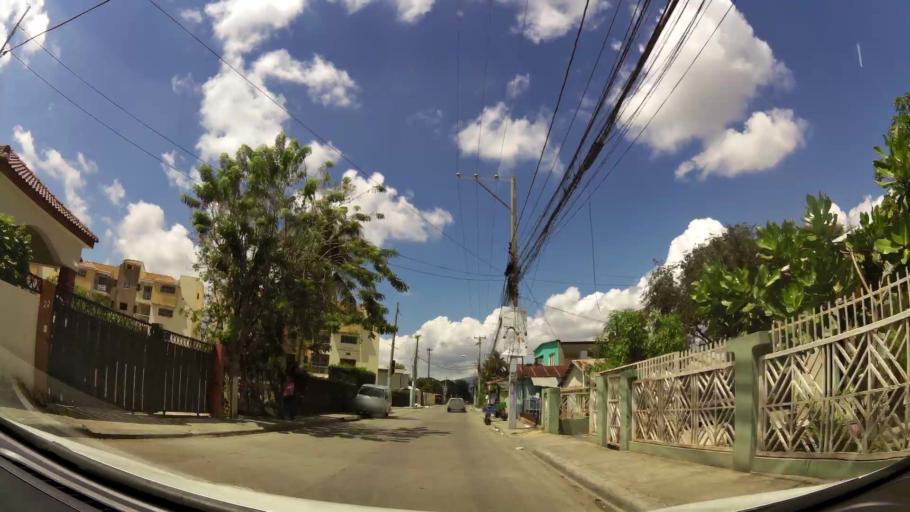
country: DO
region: Santiago
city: Santiago de los Caballeros
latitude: 19.4734
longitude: -70.6668
